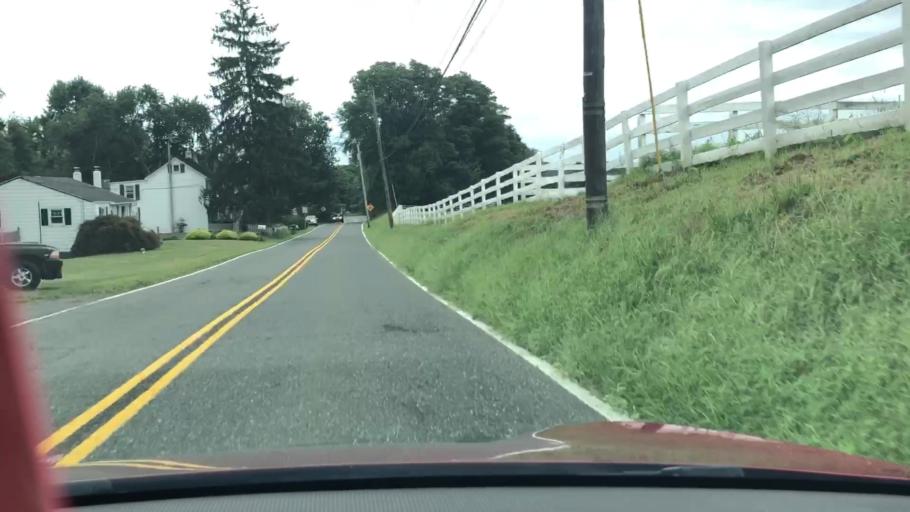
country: US
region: New Jersey
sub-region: Monmouth County
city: Shrewsbury
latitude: 40.1697
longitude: -74.5142
